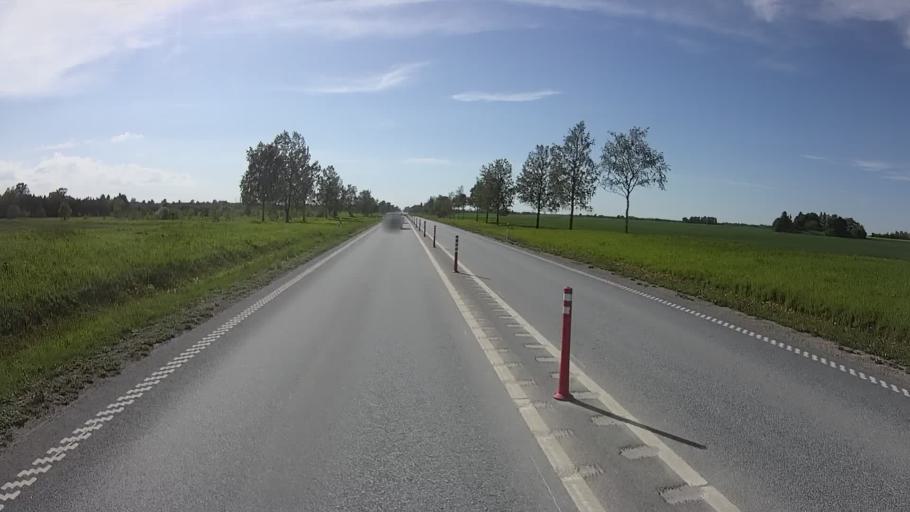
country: EE
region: Laeaene-Virumaa
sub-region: Haljala vald
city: Haljala
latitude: 59.4288
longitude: 26.2270
